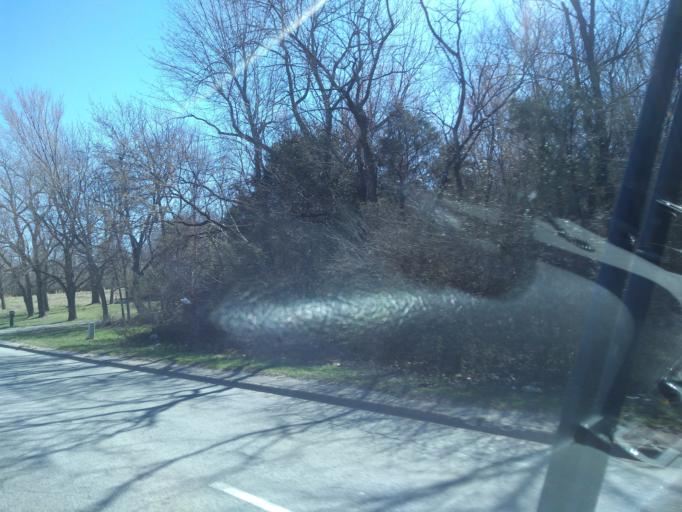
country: US
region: Arkansas
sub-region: Washington County
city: Farmington
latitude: 36.0471
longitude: -94.2236
